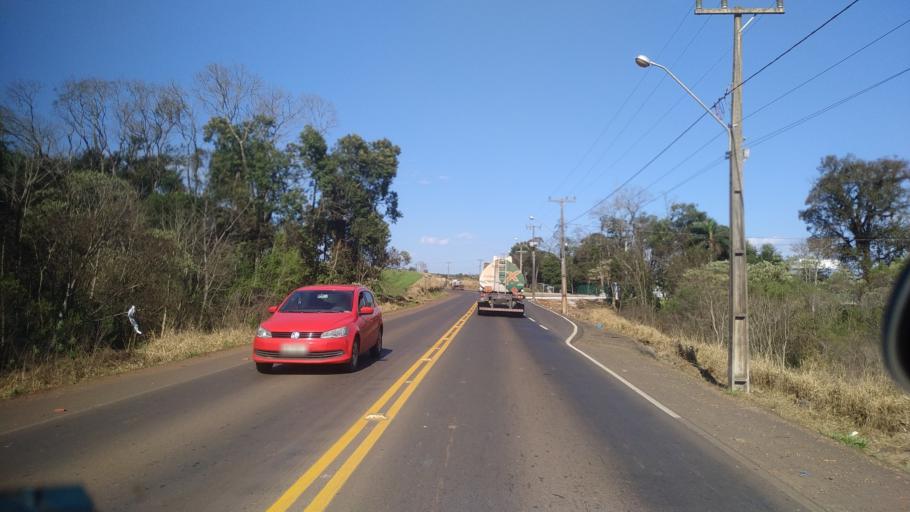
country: BR
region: Santa Catarina
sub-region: Chapeco
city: Chapeco
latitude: -27.1205
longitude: -52.6332
